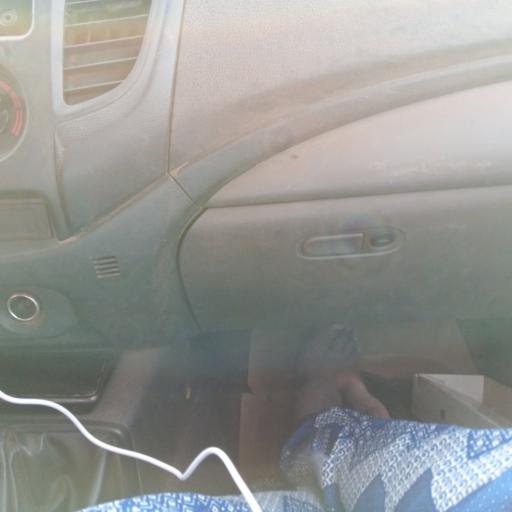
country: ML
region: Segou
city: Ke-Macina
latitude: 14.1433
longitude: -5.0636
